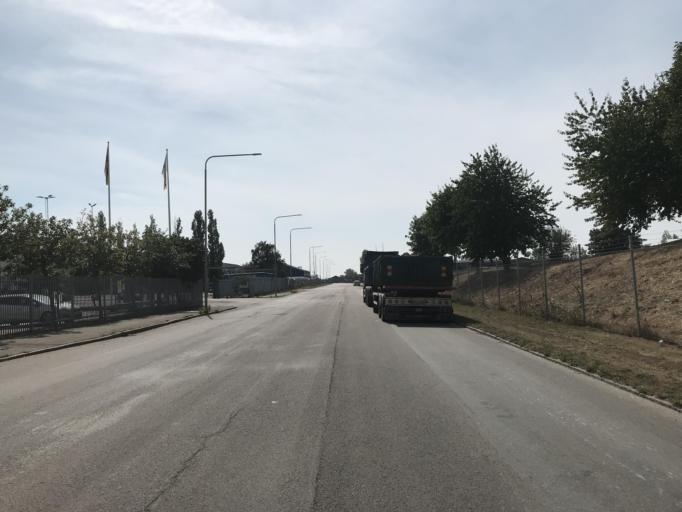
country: SE
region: Skane
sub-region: Landskrona
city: Landskrona
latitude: 55.8644
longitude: 12.8508
